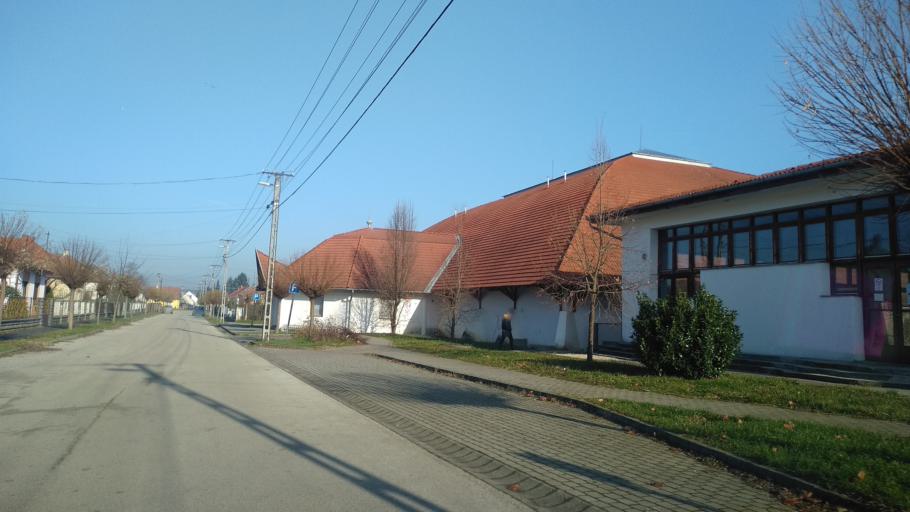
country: HU
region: Somogy
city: Barcs
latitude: 45.9628
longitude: 17.4529
